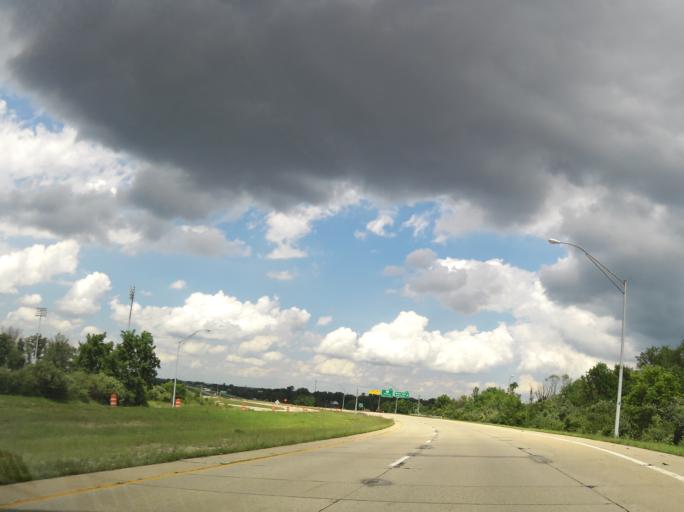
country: US
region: Ohio
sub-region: Greene County
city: Wright-Patterson AFB
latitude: 39.7833
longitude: -84.0457
